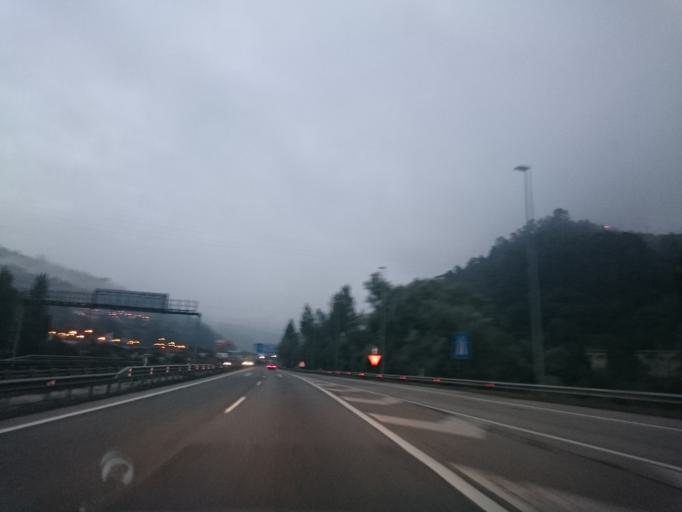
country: ES
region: Asturias
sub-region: Province of Asturias
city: Mieres
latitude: 43.2697
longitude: -5.8040
